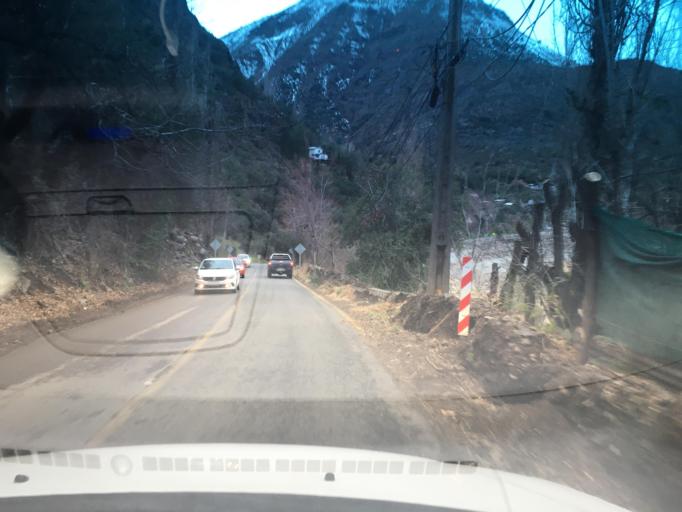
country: CL
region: Santiago Metropolitan
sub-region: Provincia de Cordillera
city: Puente Alto
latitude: -33.7330
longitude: -70.3053
